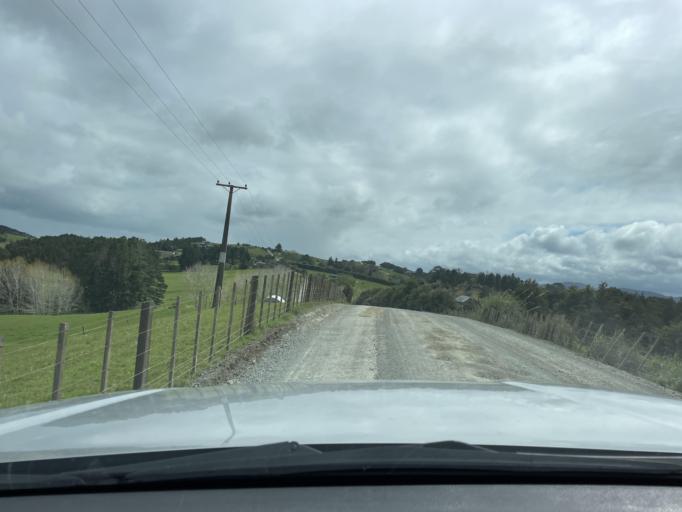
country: NZ
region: Auckland
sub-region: Auckland
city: Wellsford
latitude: -36.1724
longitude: 174.5725
